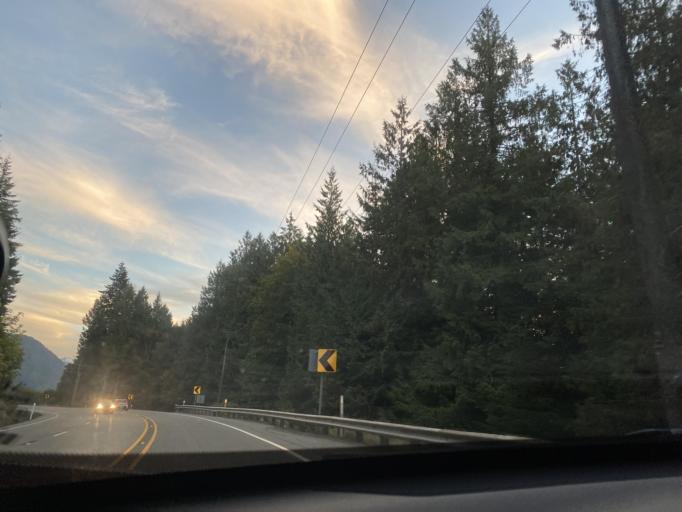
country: US
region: Washington
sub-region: Clallam County
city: Port Angeles
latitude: 48.0887
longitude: -123.5594
